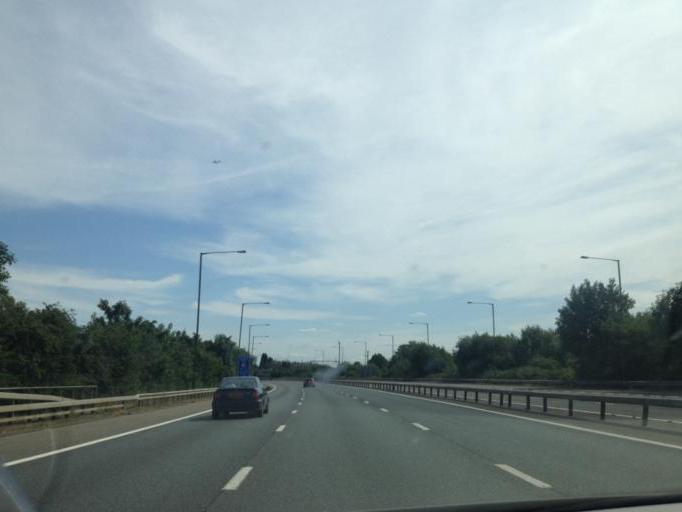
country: GB
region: England
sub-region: Greater London
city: Edgware
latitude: 51.6290
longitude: -0.2623
